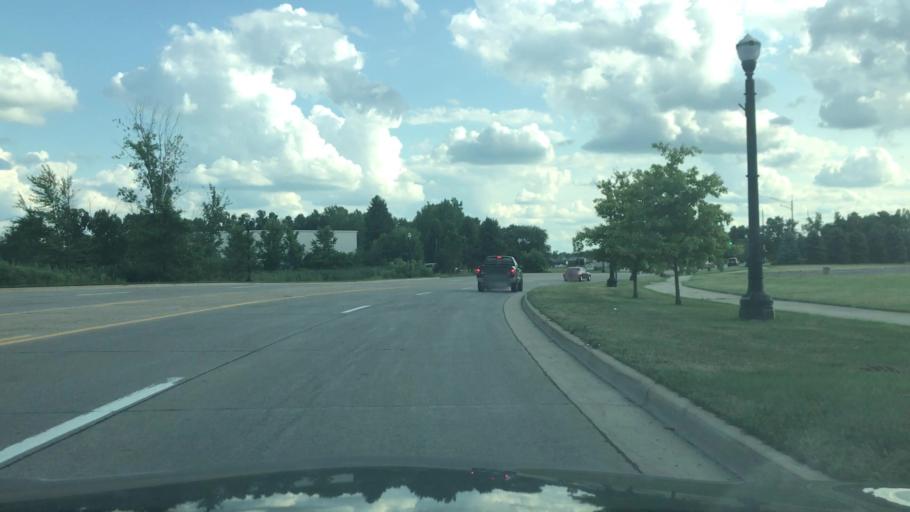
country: US
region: Michigan
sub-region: Oakland County
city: Wixom
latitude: 42.5231
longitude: -83.5361
